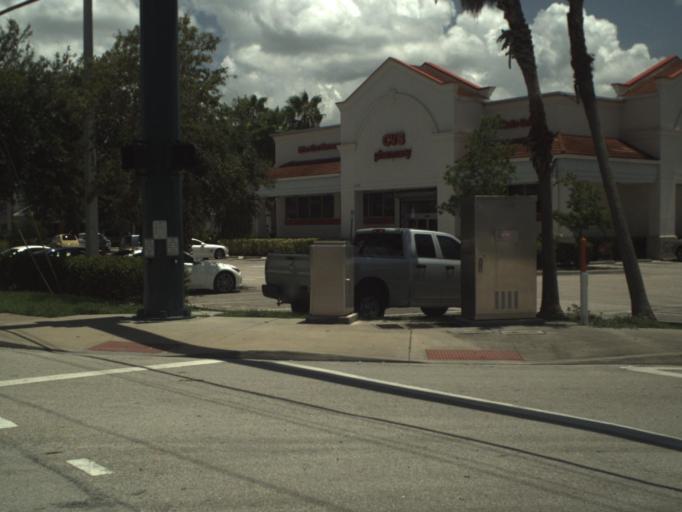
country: US
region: Florida
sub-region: Martin County
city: Stuart
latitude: 27.1778
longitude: -80.2368
